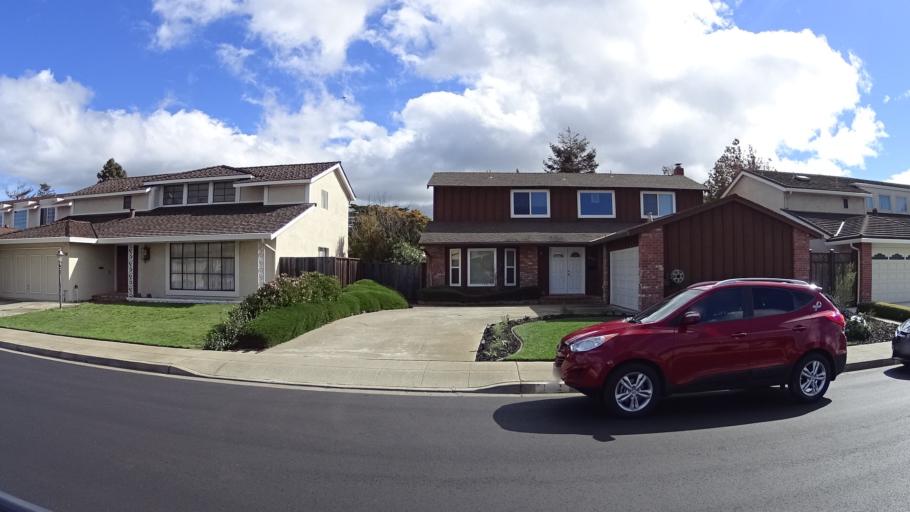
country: US
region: California
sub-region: San Mateo County
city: Foster City
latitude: 37.5680
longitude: -122.2551
